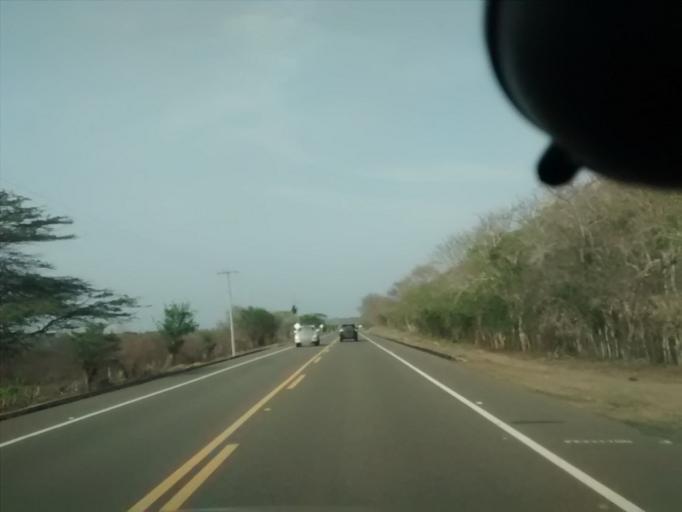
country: CO
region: Bolivar
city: Clemencia
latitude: 10.6261
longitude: -75.4347
